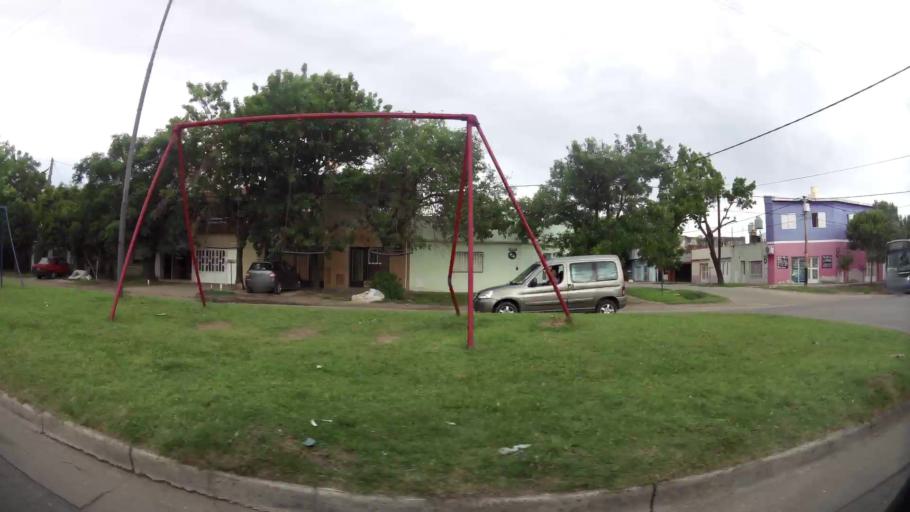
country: AR
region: Santa Fe
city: Gobernador Galvez
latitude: -32.9994
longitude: -60.6779
